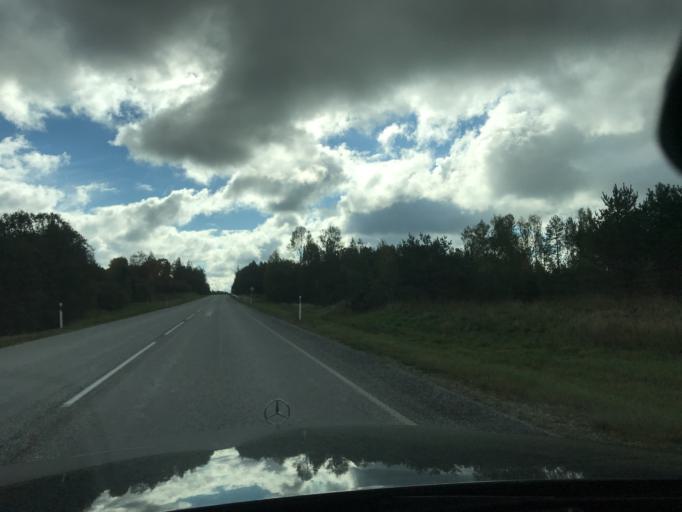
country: RU
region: Pskov
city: Pechory
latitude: 57.7028
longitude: 27.3242
